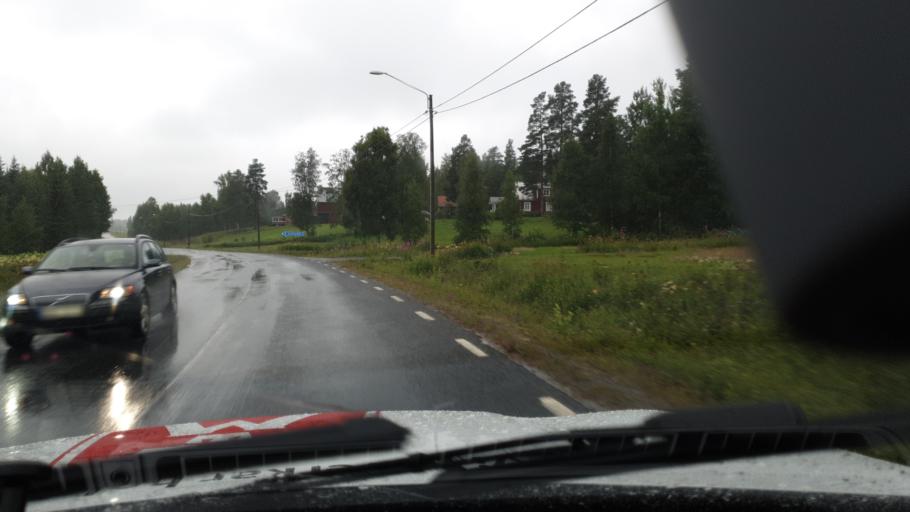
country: SE
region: Vaesterbotten
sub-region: Skelleftea Kommun
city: Soedra Bergsbyn
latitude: 64.5819
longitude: 21.0004
